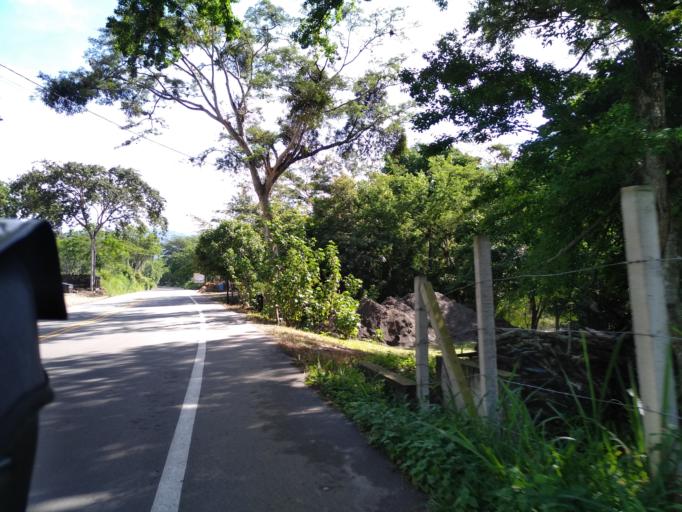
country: CO
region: Santander
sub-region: San Gil
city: San Gil
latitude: 6.5195
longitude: -73.1253
